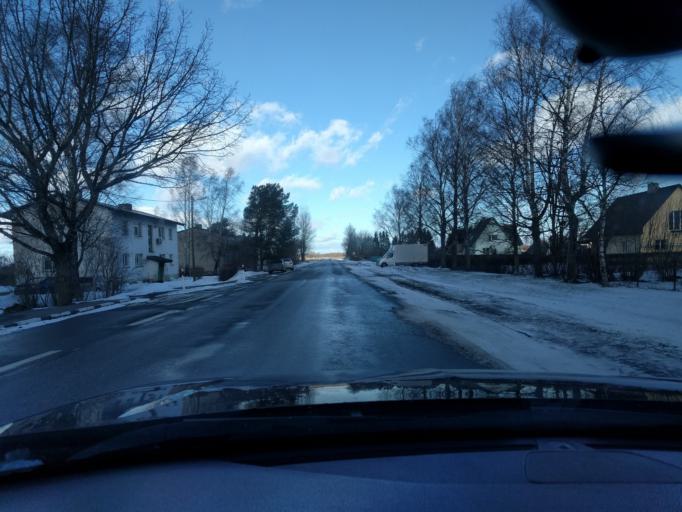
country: EE
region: Harju
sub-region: Raasiku vald
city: Raasiku
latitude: 59.3371
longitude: 25.1533
